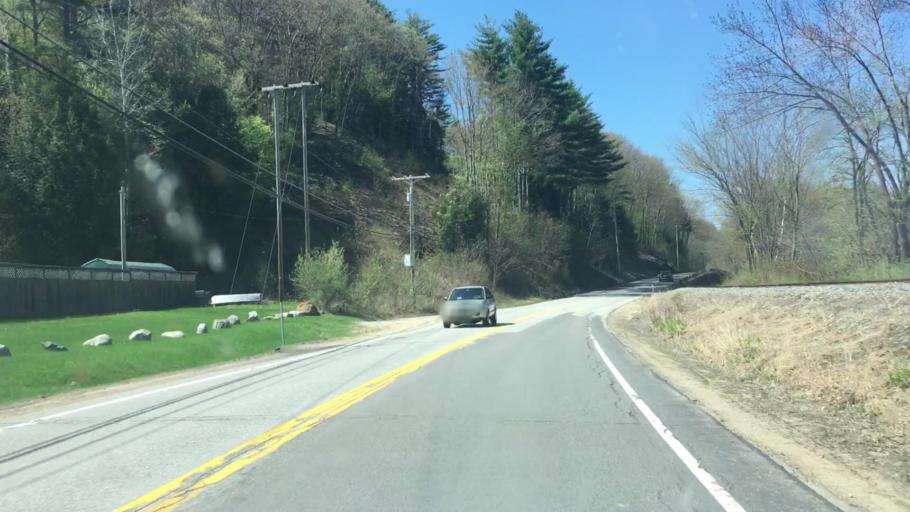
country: US
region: New Hampshire
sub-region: Grafton County
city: Plymouth
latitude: 43.7405
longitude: -71.6780
